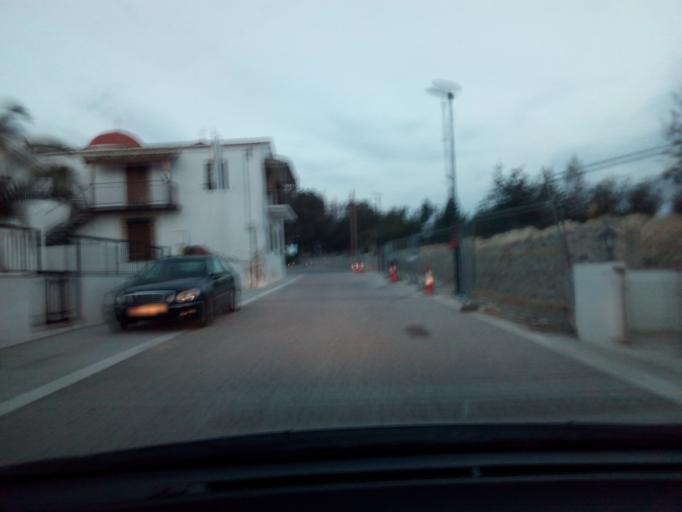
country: CY
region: Larnaka
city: Kofinou
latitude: 34.8254
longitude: 33.4638
